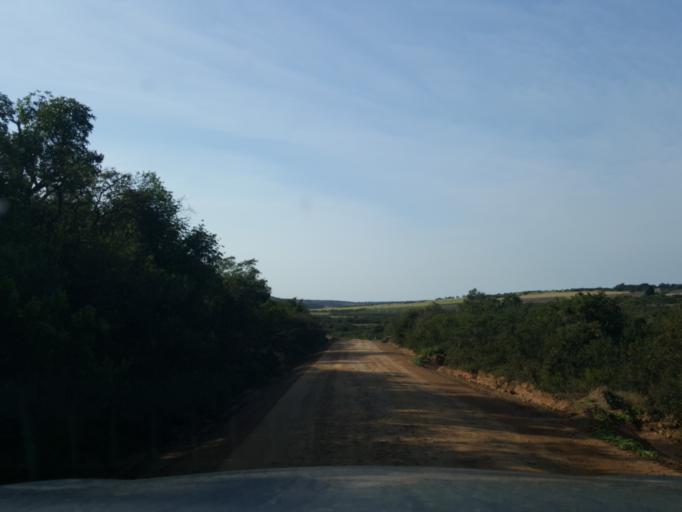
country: ZA
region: Eastern Cape
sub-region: Cacadu District Municipality
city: Grahamstown
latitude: -33.4103
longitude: 26.3045
